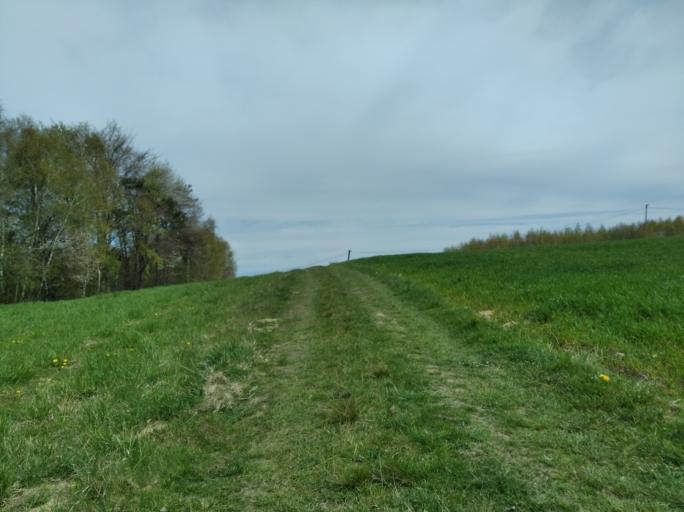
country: PL
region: Subcarpathian Voivodeship
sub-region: Powiat ropczycko-sedziszowski
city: Wielopole Skrzynskie
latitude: 49.9127
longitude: 21.6119
